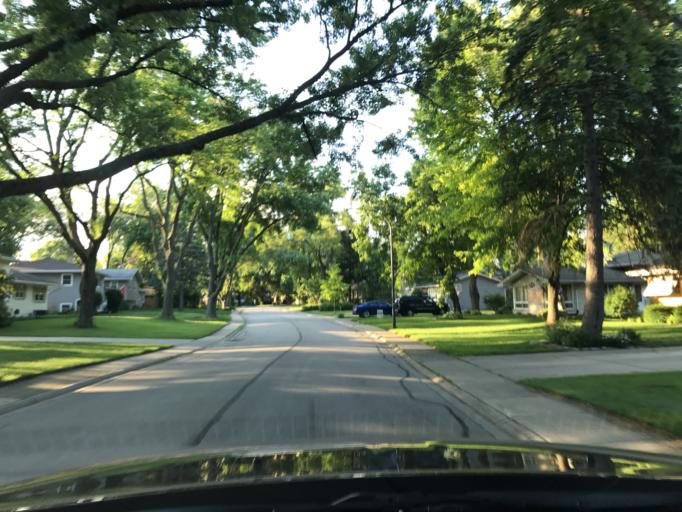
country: US
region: Illinois
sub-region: DuPage County
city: Naperville
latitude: 41.7554
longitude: -88.1567
